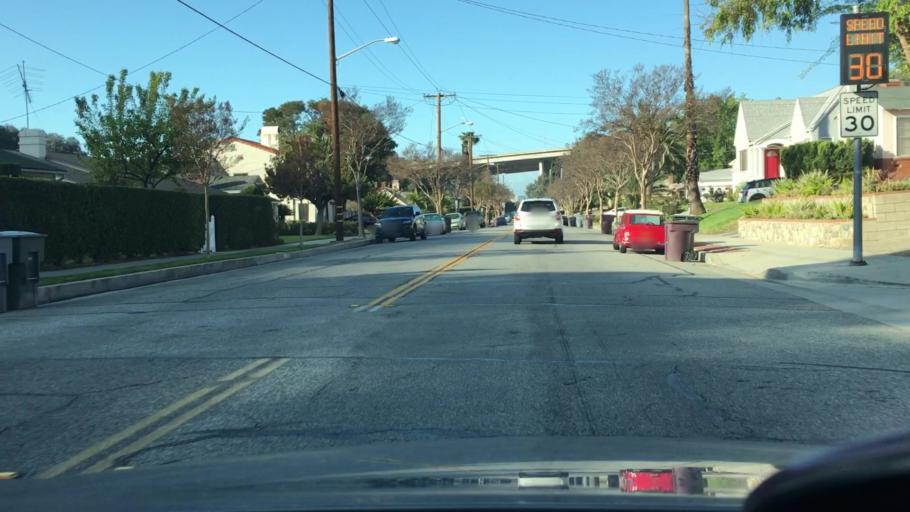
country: US
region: California
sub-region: Los Angeles County
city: Glendale
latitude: 34.1579
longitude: -118.2201
